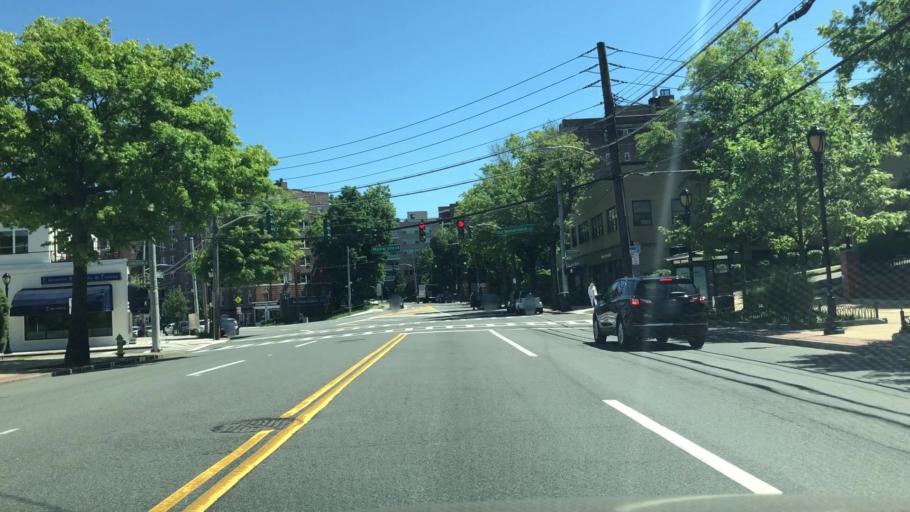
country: US
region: New York
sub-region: Westchester County
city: White Plains
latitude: 41.0246
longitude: -73.7633
